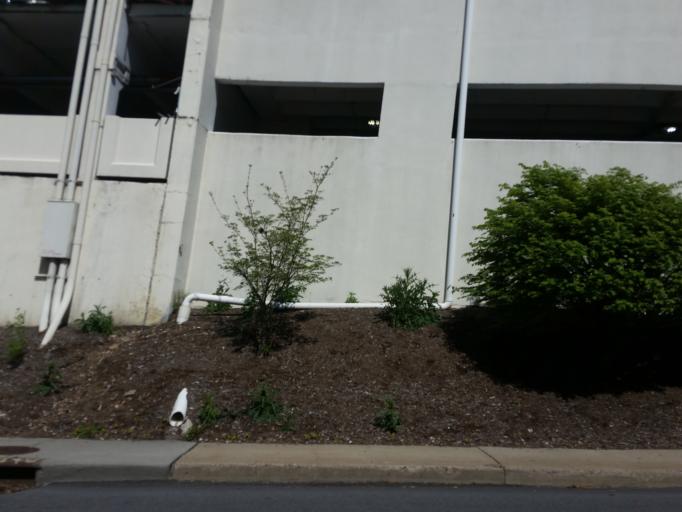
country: US
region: North Carolina
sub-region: Buncombe County
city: Asheville
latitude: 35.5807
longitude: -82.5508
